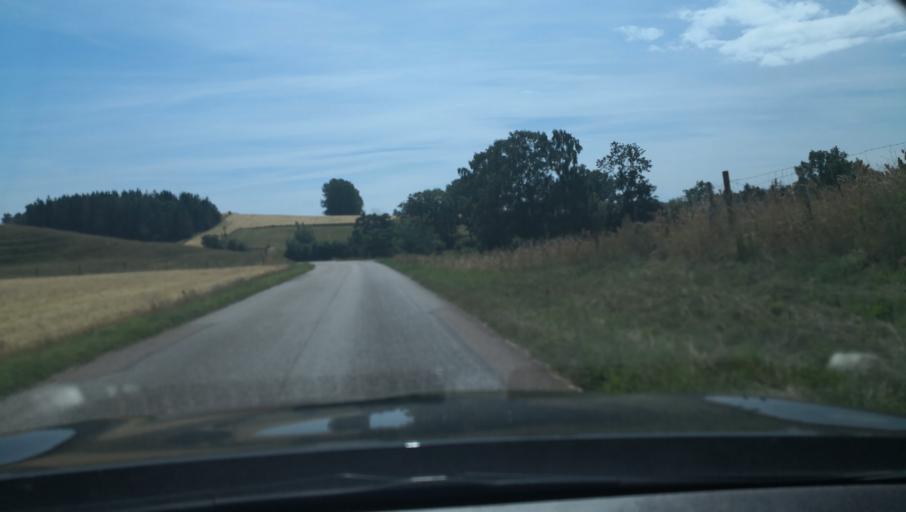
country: SE
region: Skane
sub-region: Ystads Kommun
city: Kopingebro
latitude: 55.3931
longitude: 14.1382
